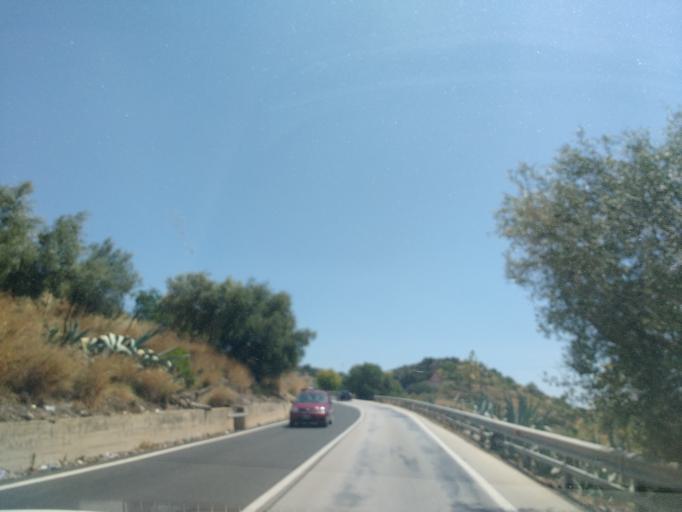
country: IT
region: Sicily
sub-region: Provincia di Siracusa
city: Noto
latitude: 36.8674
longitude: 15.0310
